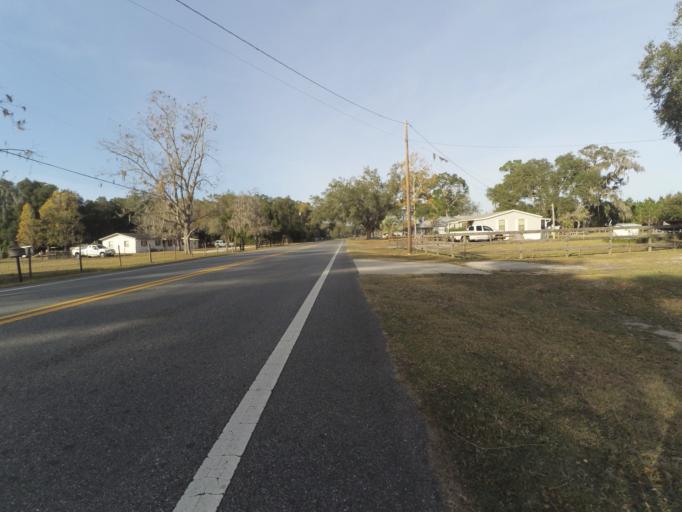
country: US
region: Florida
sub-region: Lake County
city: Umatilla
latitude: 28.9640
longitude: -81.6421
